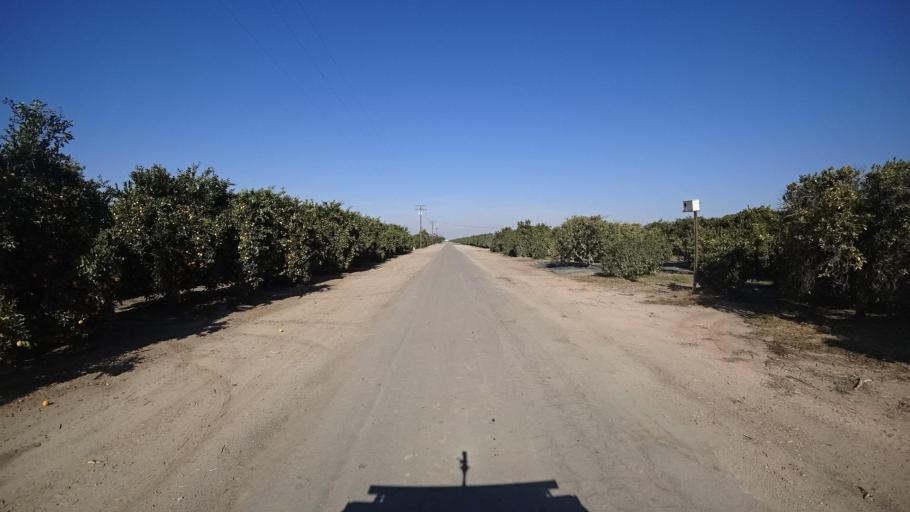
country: US
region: California
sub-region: Tulare County
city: Richgrove
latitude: 35.7265
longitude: -119.1429
